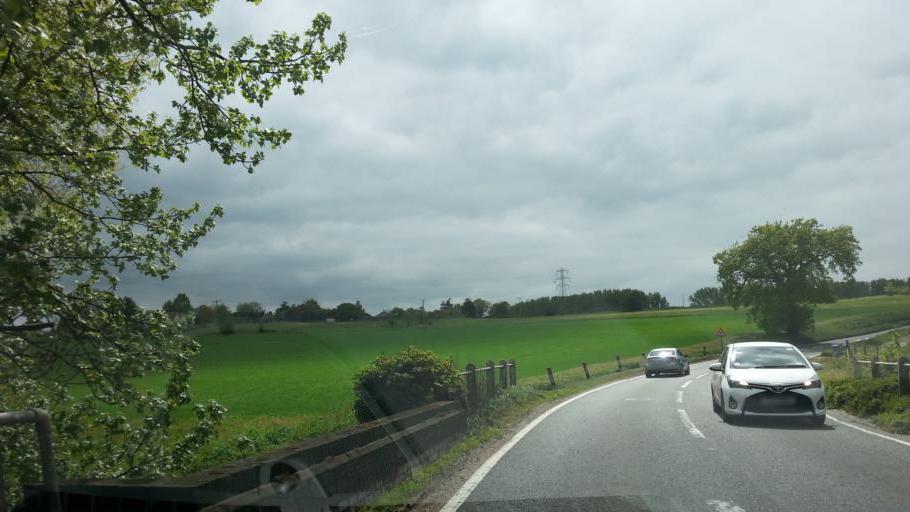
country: GB
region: England
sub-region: Suffolk
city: Bramford
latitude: 52.0503
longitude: 1.0665
